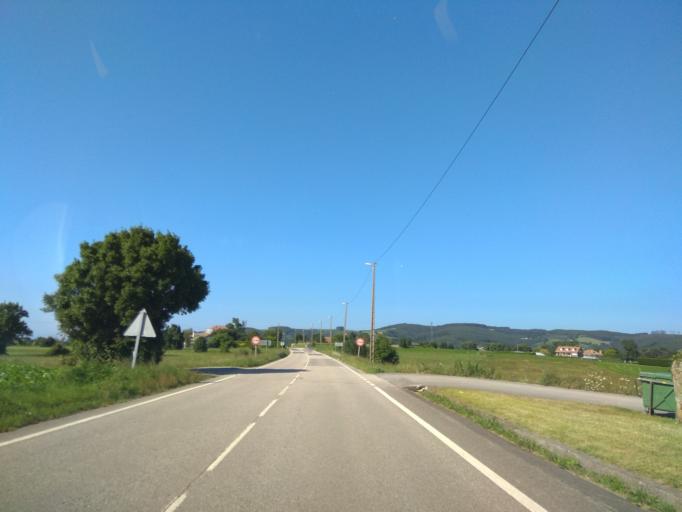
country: ES
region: Cantabria
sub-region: Provincia de Cantabria
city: Bareyo
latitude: 43.4570
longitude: -3.6756
